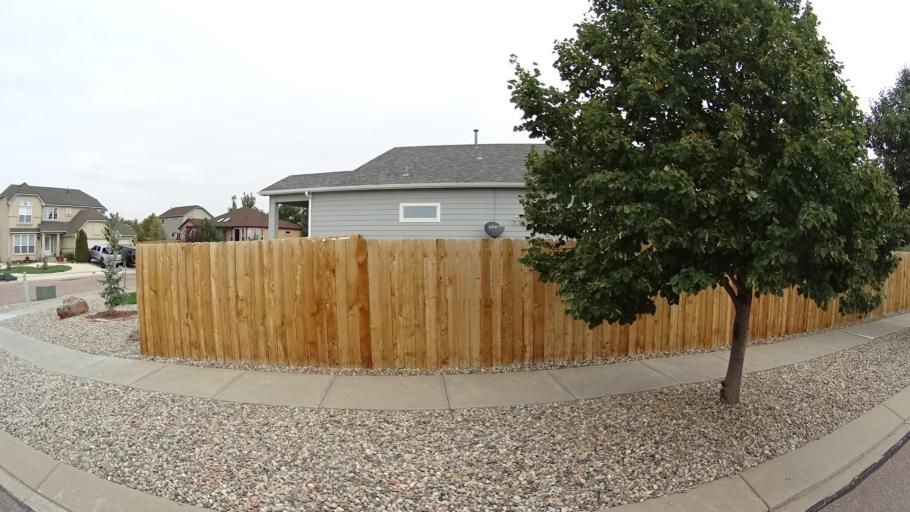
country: US
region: Colorado
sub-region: El Paso County
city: Cimarron Hills
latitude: 38.9141
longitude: -104.6921
